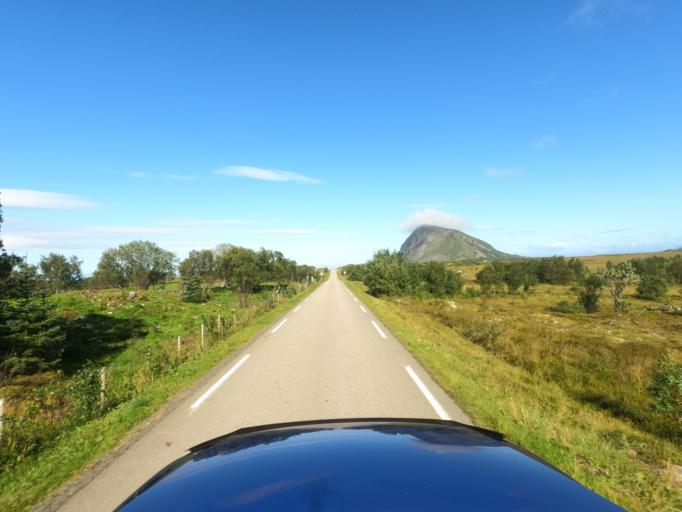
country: NO
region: Nordland
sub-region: Vestvagoy
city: Evjen
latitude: 68.3057
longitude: 14.0987
